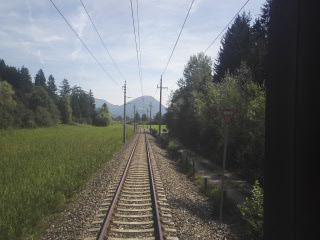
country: AT
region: Styria
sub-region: Politischer Bezirk Liezen
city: Weissenbach bei Liezen
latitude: 47.5616
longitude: 14.1835
